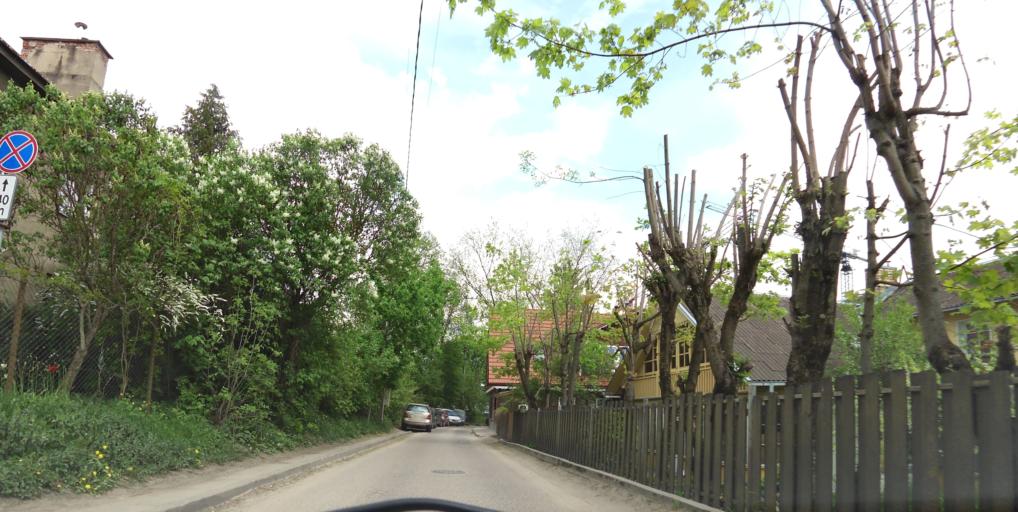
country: LT
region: Vilnius County
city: Rasos
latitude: 54.6819
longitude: 25.3034
